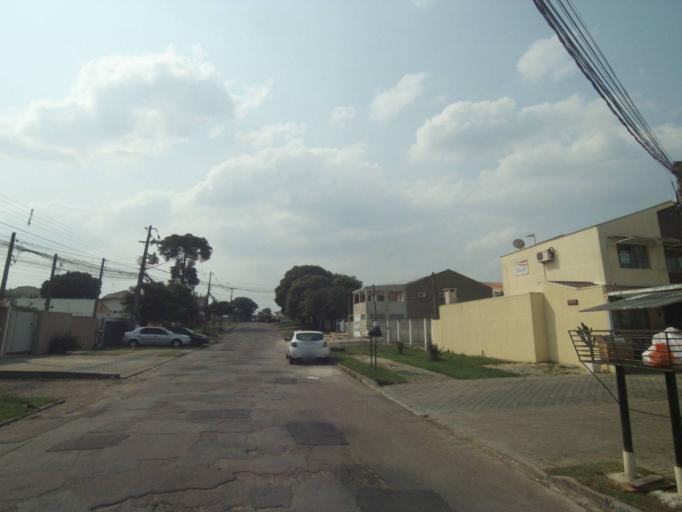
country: BR
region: Parana
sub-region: Sao Jose Dos Pinhais
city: Sao Jose dos Pinhais
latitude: -25.5290
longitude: -49.2323
